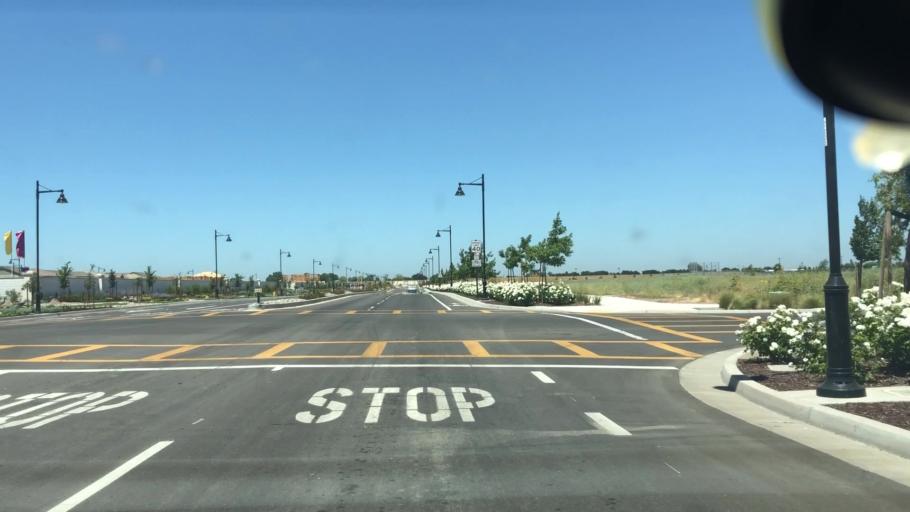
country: US
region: California
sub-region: San Joaquin County
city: Lathrop
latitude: 37.7950
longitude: -121.3224
